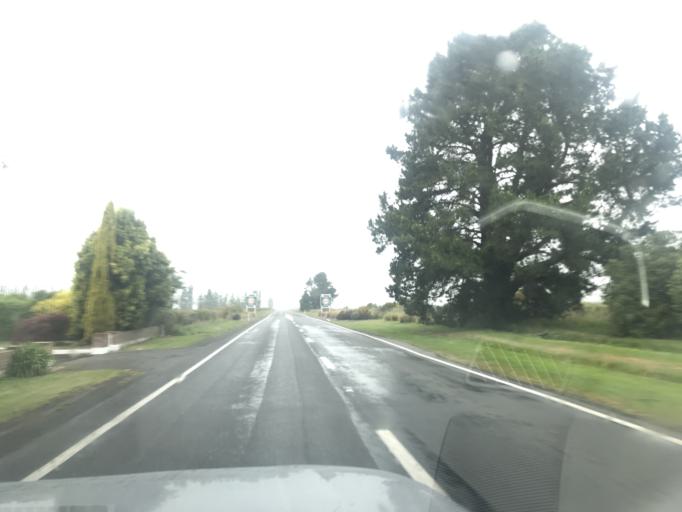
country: NZ
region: Canterbury
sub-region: Selwyn District
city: Darfield
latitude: -43.5021
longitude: 172.2188
